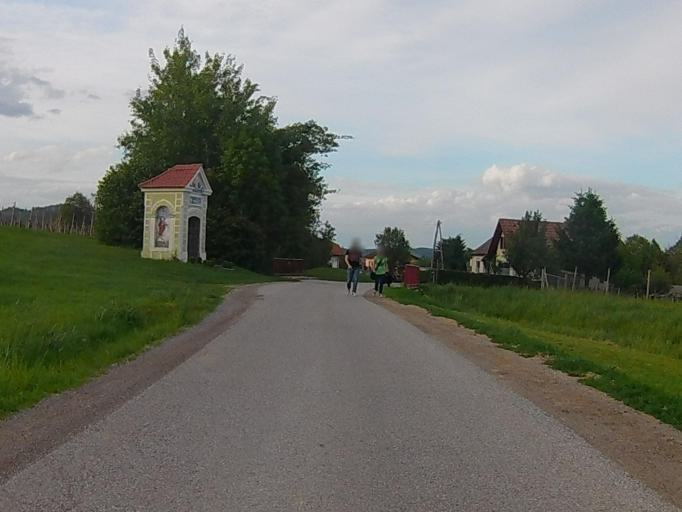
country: SI
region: Maribor
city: Pekre
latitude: 46.5441
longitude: 15.5880
